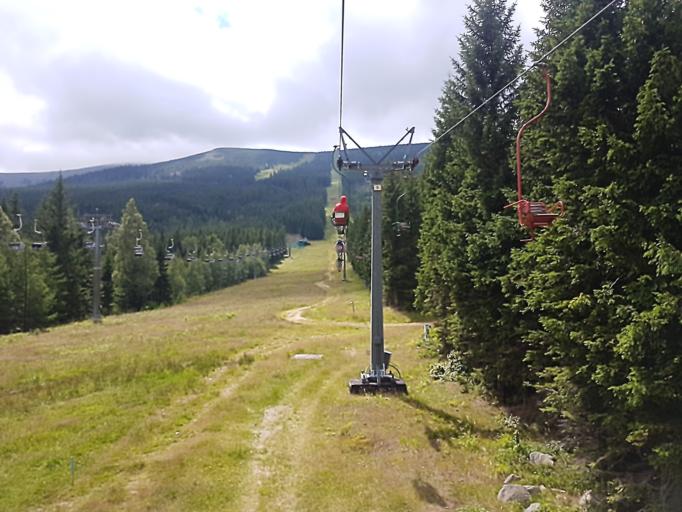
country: PL
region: Lower Silesian Voivodeship
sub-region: Powiat jeleniogorski
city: Karpacz
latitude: 50.7623
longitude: 15.7287
